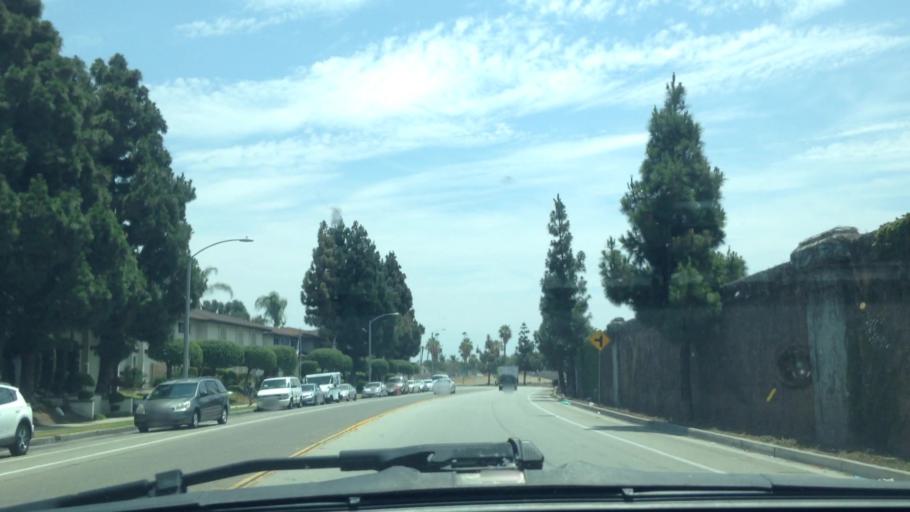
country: US
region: California
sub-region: Orange County
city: Anaheim
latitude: 33.8339
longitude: -117.9336
